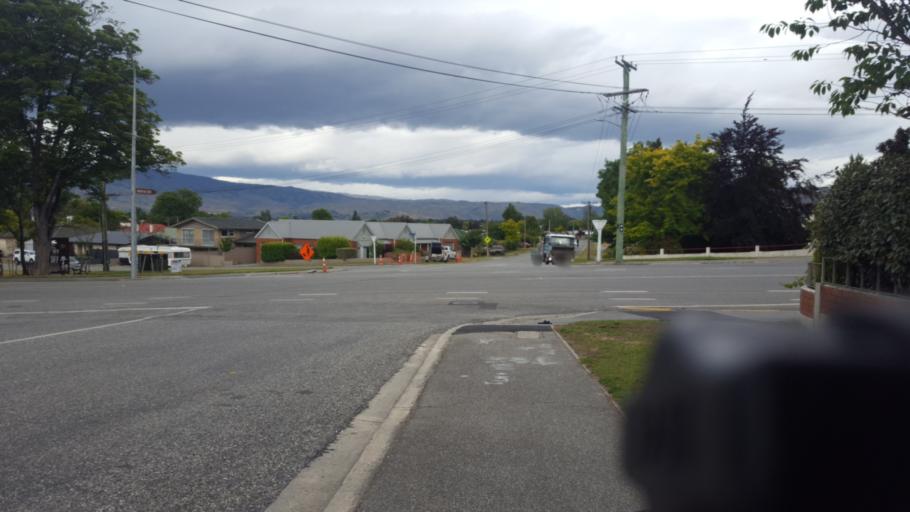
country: NZ
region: Otago
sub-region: Queenstown-Lakes District
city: Wanaka
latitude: -45.2506
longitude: 169.3968
